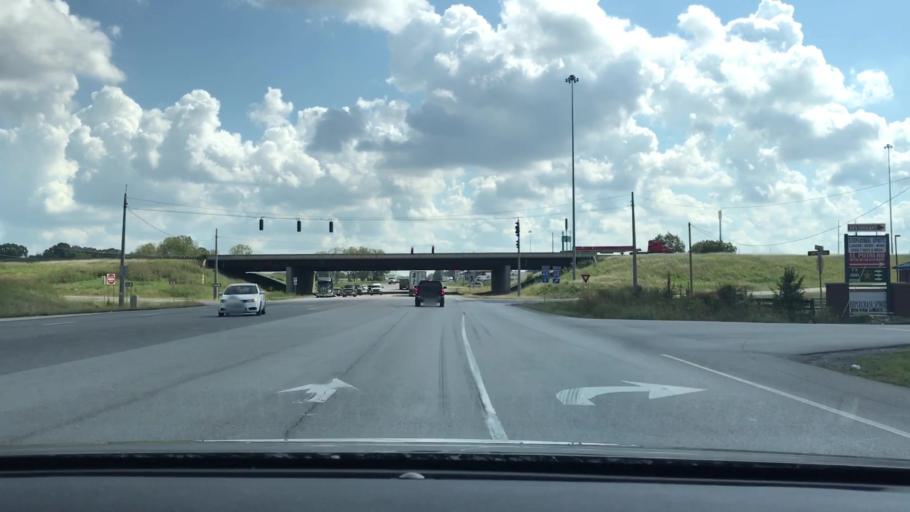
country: US
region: Kentucky
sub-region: Simpson County
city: Franklin
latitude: 36.7166
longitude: -86.5240
